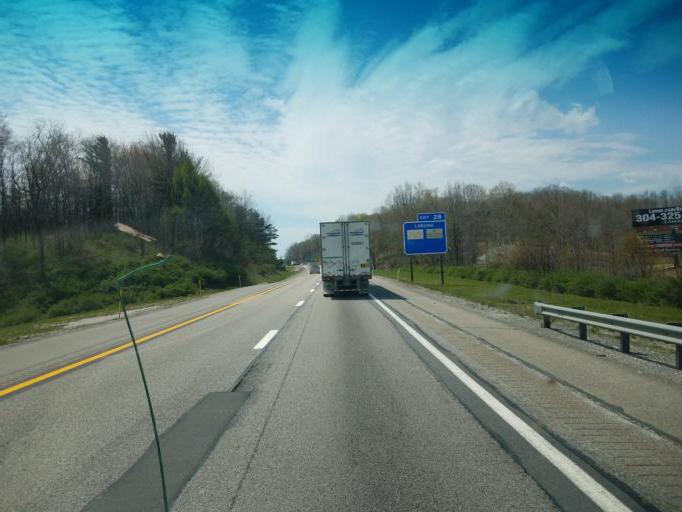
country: US
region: West Virginia
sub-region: Raleigh County
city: Shady Spring
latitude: 37.6245
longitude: -81.1173
